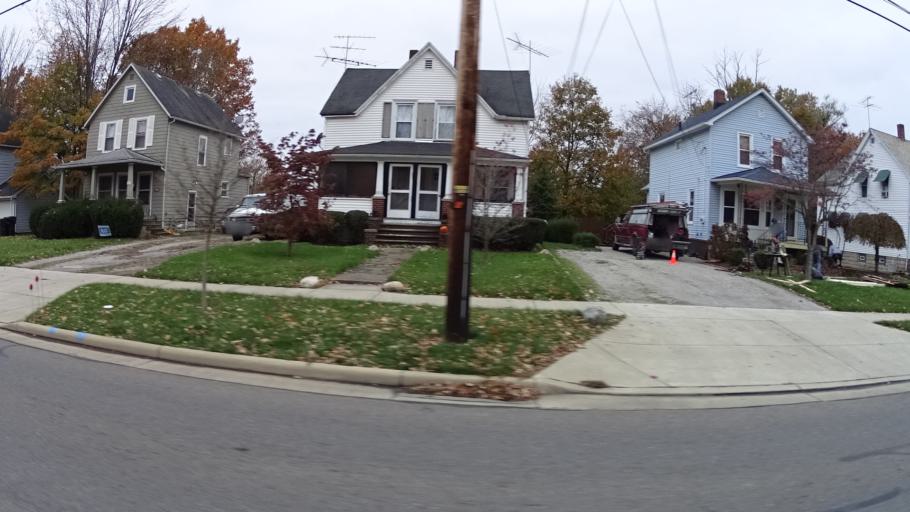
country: US
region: Ohio
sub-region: Lorain County
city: Elyria
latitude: 41.3566
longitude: -82.1001
